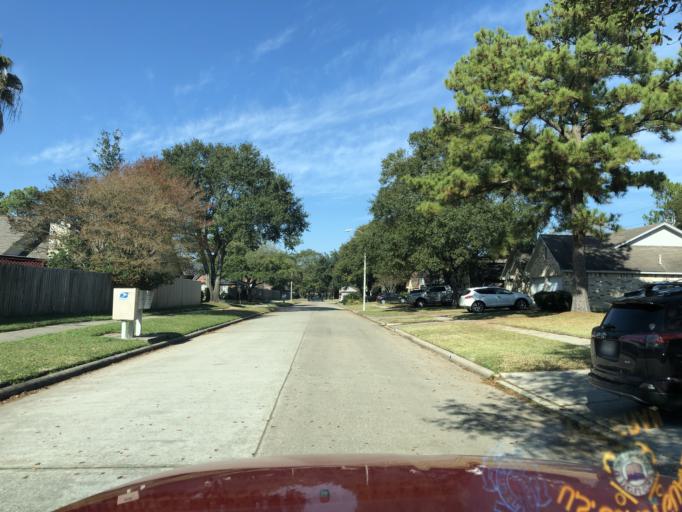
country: US
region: Texas
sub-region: Harris County
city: Tomball
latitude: 30.0200
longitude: -95.5566
